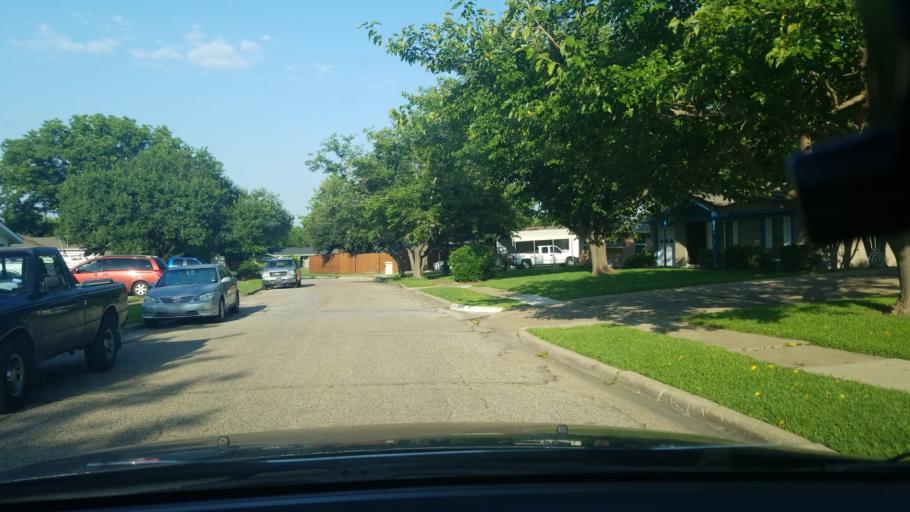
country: US
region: Texas
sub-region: Dallas County
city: Mesquite
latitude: 32.8119
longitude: -96.6407
